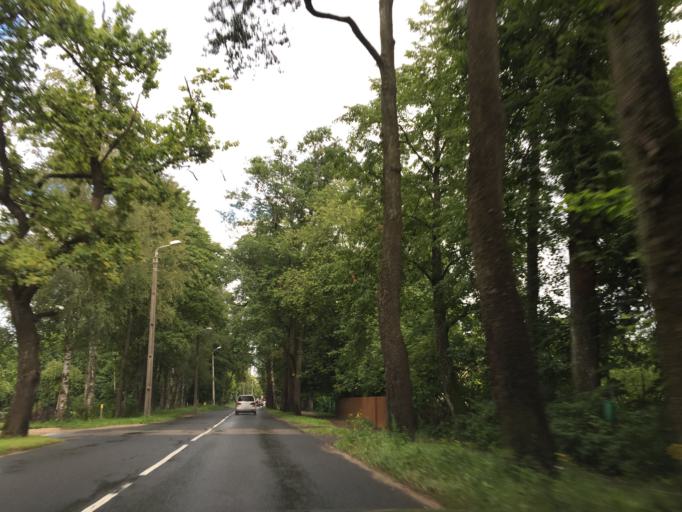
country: LV
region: Marupe
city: Marupe
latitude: 56.9534
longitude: 23.9919
